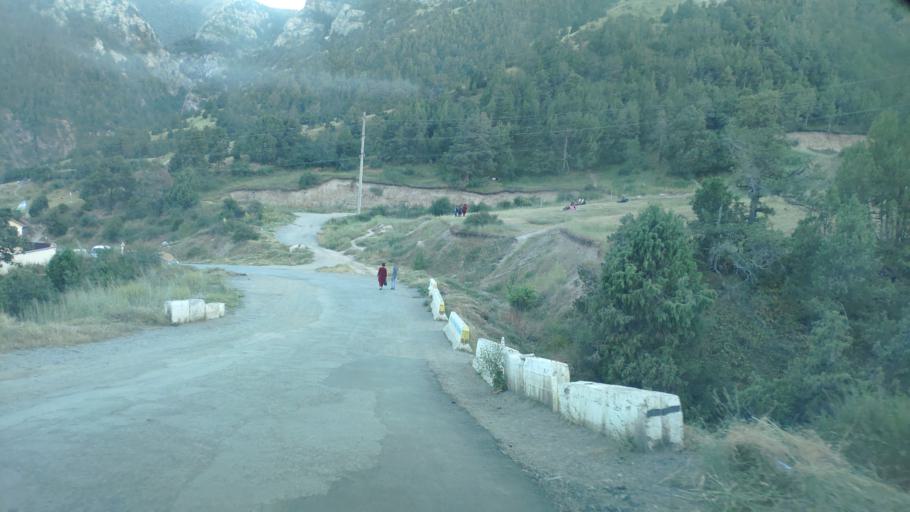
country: TJ
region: Viloyati Sughd
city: Ayni
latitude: 39.6343
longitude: 68.4910
